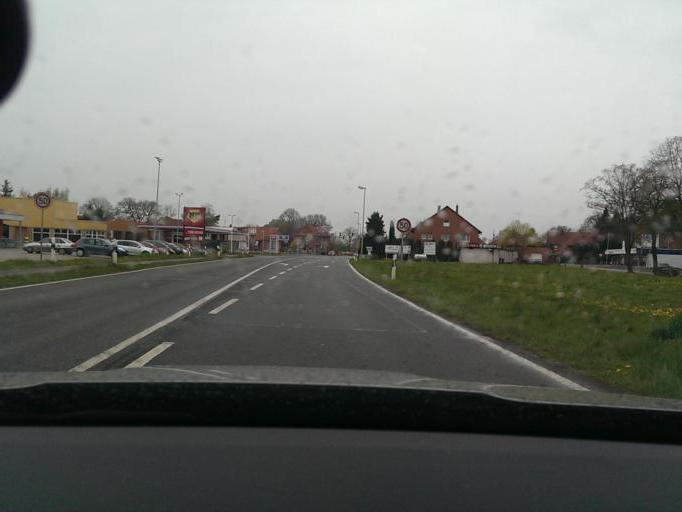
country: DE
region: Lower Saxony
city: Steimbke
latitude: 52.6635
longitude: 9.4860
